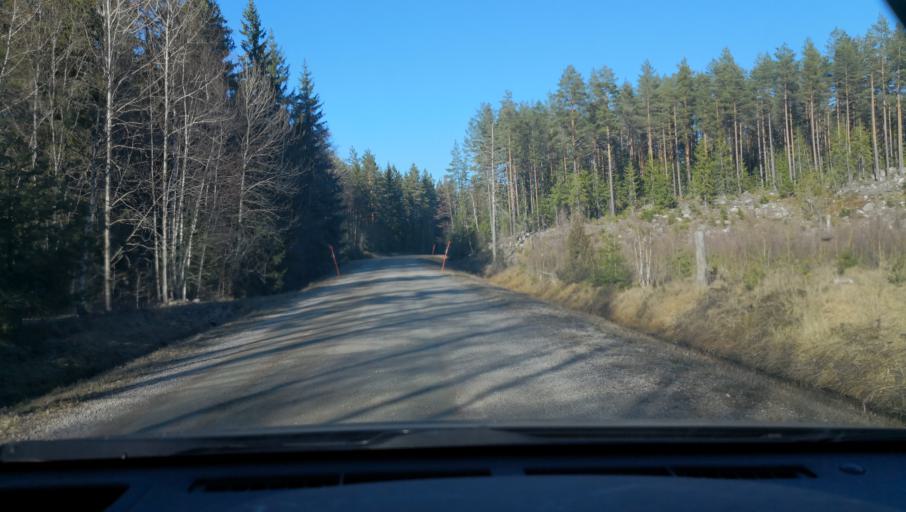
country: SE
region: Vaestmanland
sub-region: Sala Kommun
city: Sala
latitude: 60.1636
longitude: 16.6310
